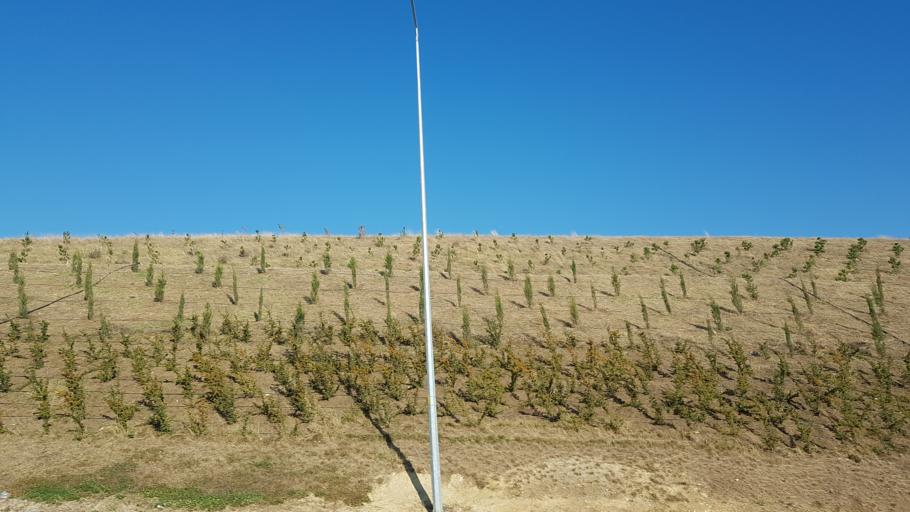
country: TR
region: Balikesir
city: Ertugrul
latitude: 39.6587
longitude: 27.7322
